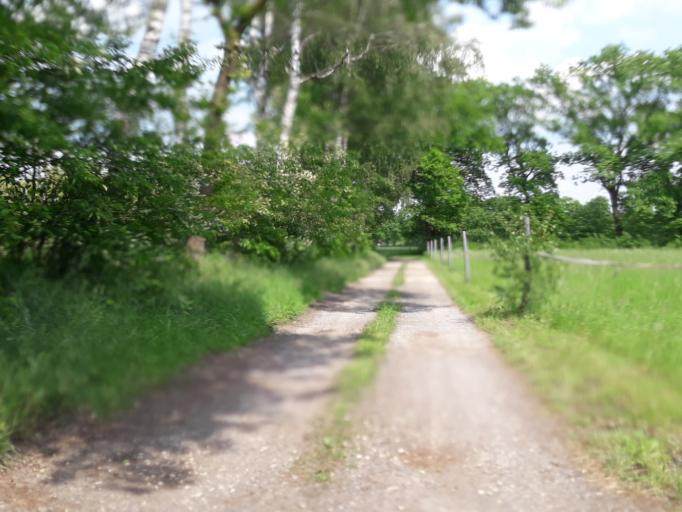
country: DE
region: North Rhine-Westphalia
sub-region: Regierungsbezirk Detmold
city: Paderborn
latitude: 51.7607
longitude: 8.7562
